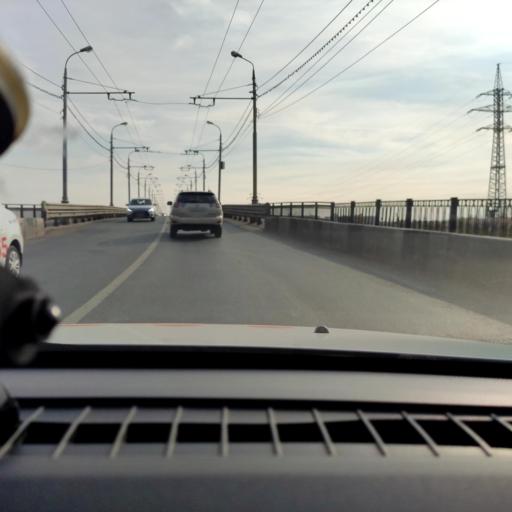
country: RU
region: Samara
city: Rozhdestveno
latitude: 53.1749
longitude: 50.0731
